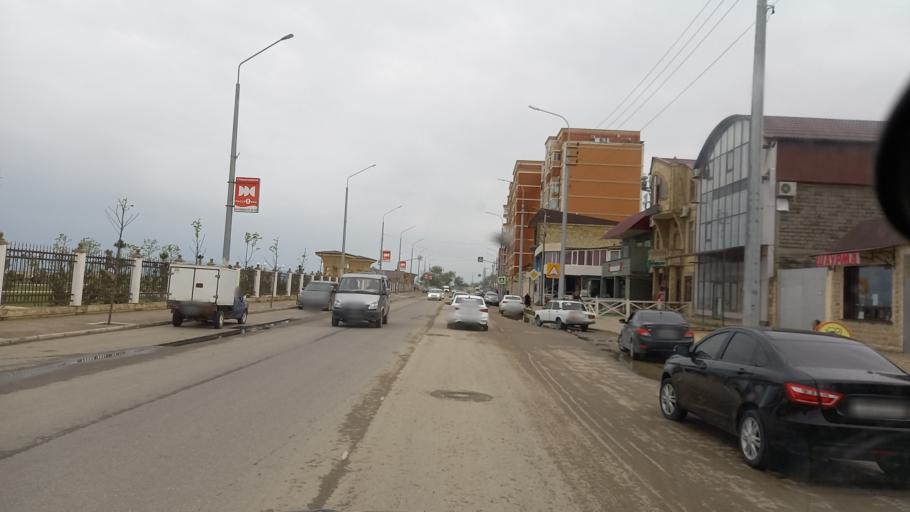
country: RU
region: Dagestan
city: Derbent
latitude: 42.0888
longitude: 48.2908
